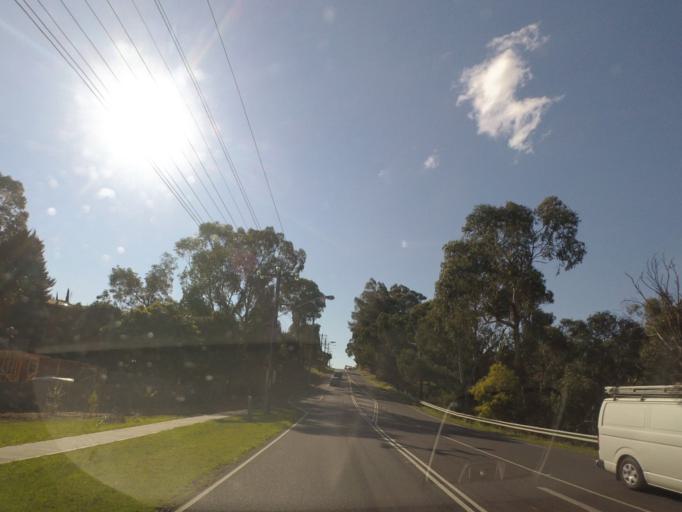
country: AU
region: Victoria
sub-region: Manningham
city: Donvale
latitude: -37.7758
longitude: 145.1829
